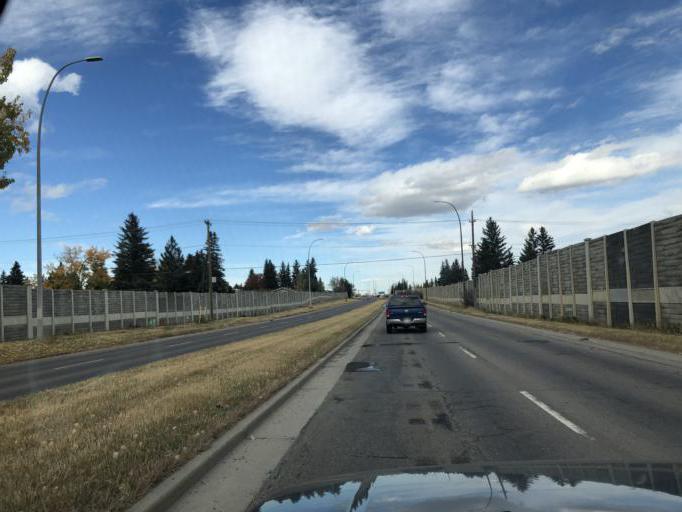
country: CA
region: Alberta
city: Calgary
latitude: 50.9567
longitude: -114.0947
